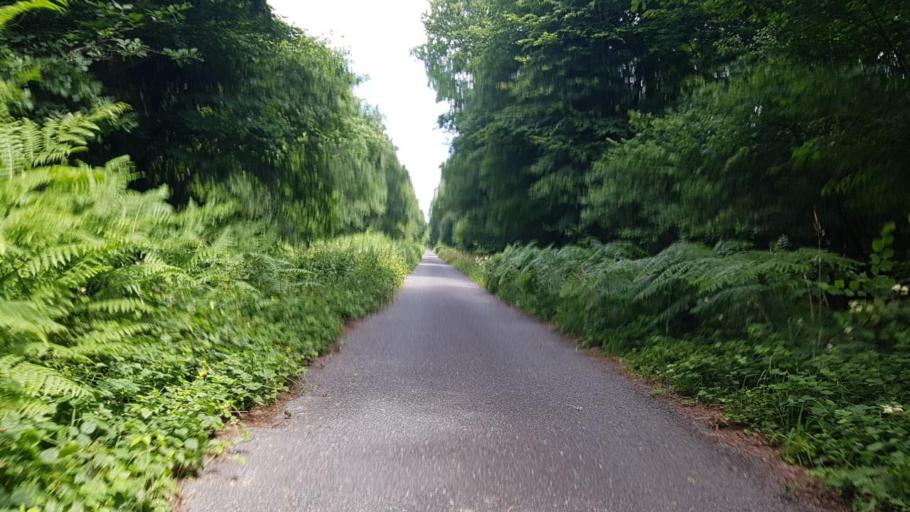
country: FR
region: Picardie
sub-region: Departement de l'Oise
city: Montmacq
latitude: 49.4675
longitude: 2.9116
